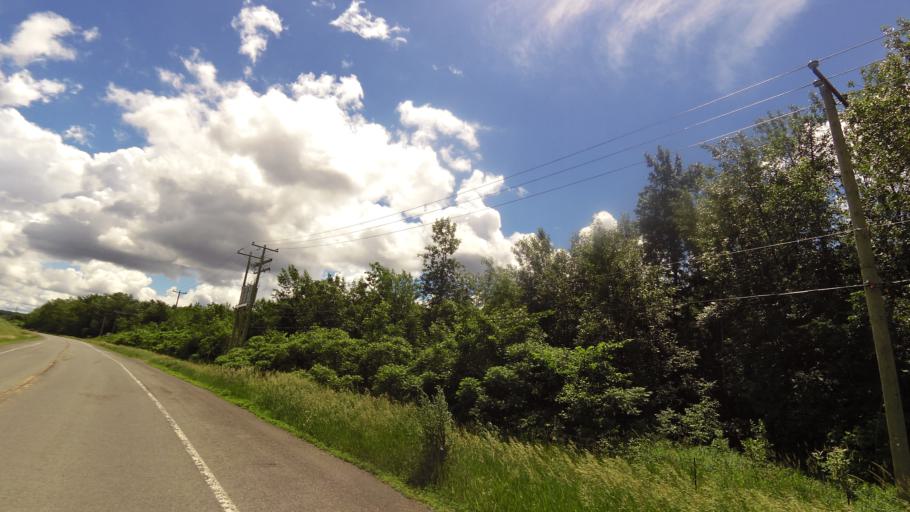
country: CA
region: Quebec
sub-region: Monteregie
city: Rigaud
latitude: 45.5374
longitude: -74.3292
